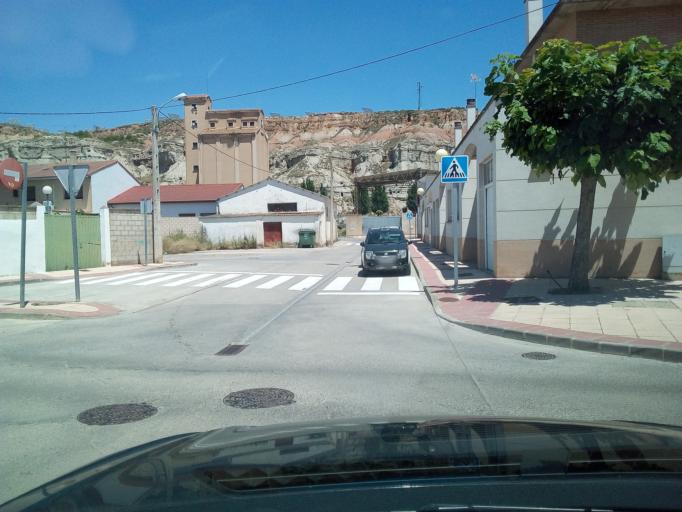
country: ES
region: Navarre
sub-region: Provincia de Navarra
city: Arguedas
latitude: 42.1727
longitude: -1.5935
